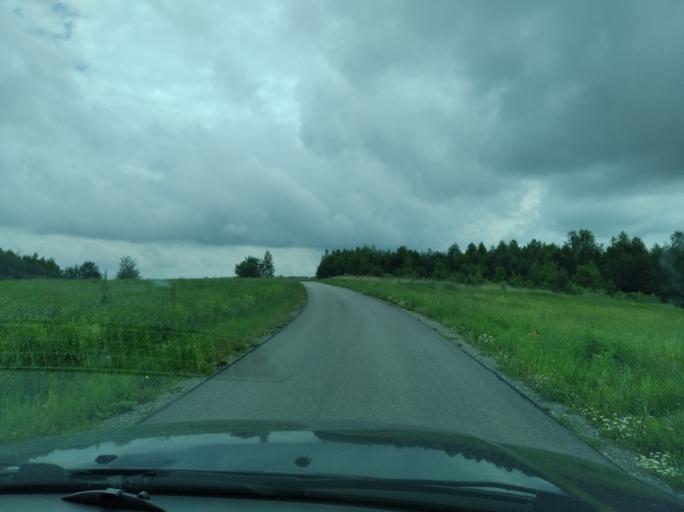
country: PL
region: Subcarpathian Voivodeship
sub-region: Powiat przemyski
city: Nienadowa
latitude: 49.8658
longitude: 22.4062
